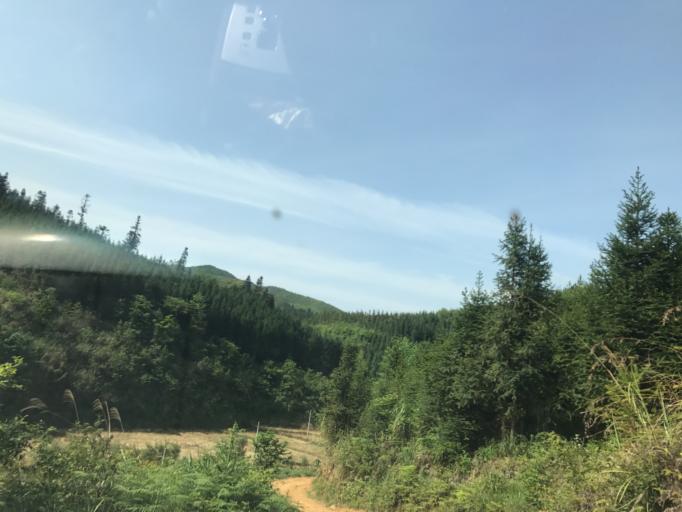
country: CN
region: Guangxi Zhuangzu Zizhiqu
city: Xinzhou
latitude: 24.9468
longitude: 105.8167
